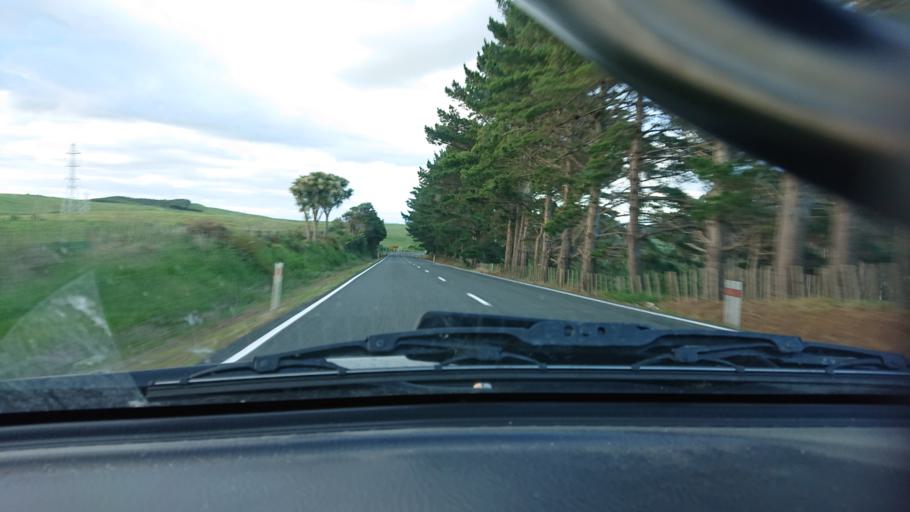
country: NZ
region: Auckland
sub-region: Auckland
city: Parakai
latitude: -36.4701
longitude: 174.4484
